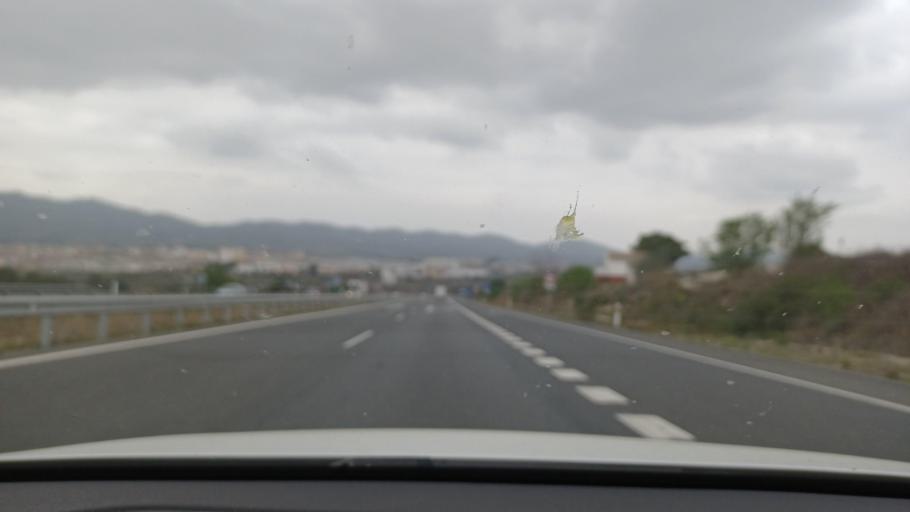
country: ES
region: Valencia
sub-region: Provincia de Valencia
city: Aielo de Malferit
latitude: 38.8676
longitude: -0.5761
